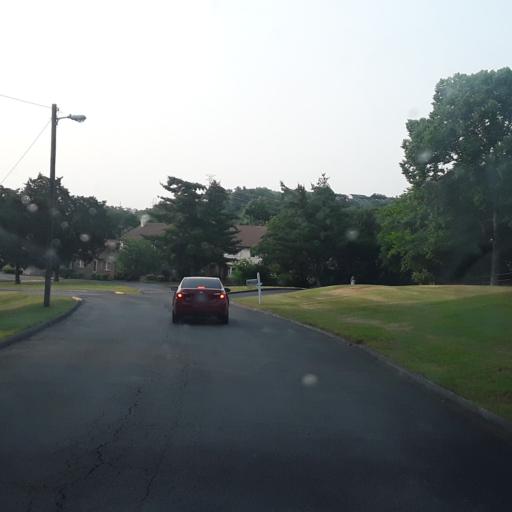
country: US
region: Tennessee
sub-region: Williamson County
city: Brentwood Estates
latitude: 36.0491
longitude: -86.7261
